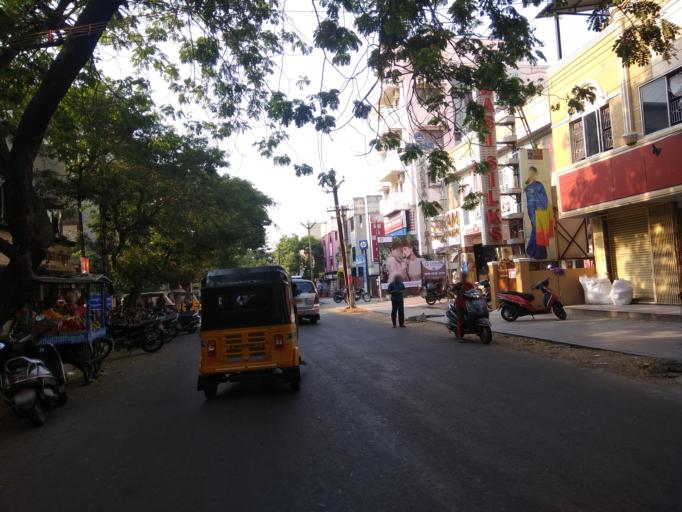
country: IN
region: Tamil Nadu
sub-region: Kancheepuram
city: Madipakkam
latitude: 12.9810
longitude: 80.1882
